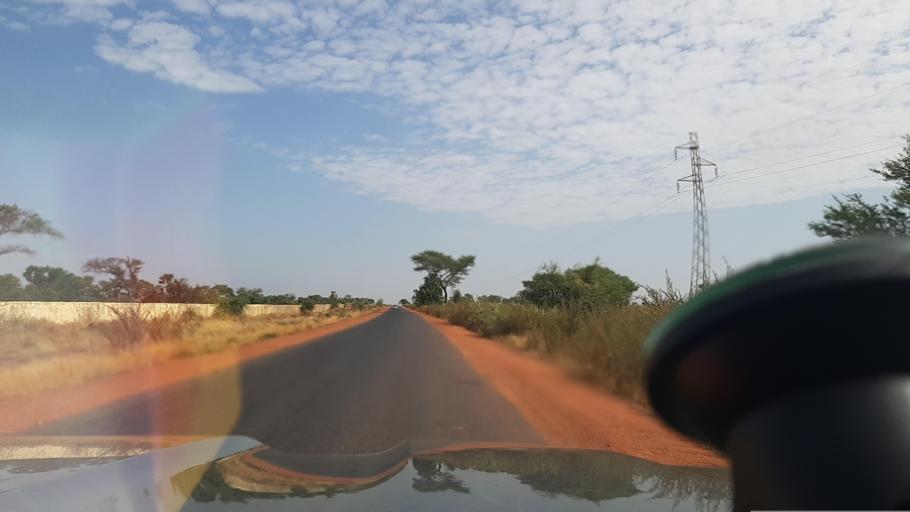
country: ML
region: Segou
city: Segou
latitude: 13.5327
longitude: -6.1258
